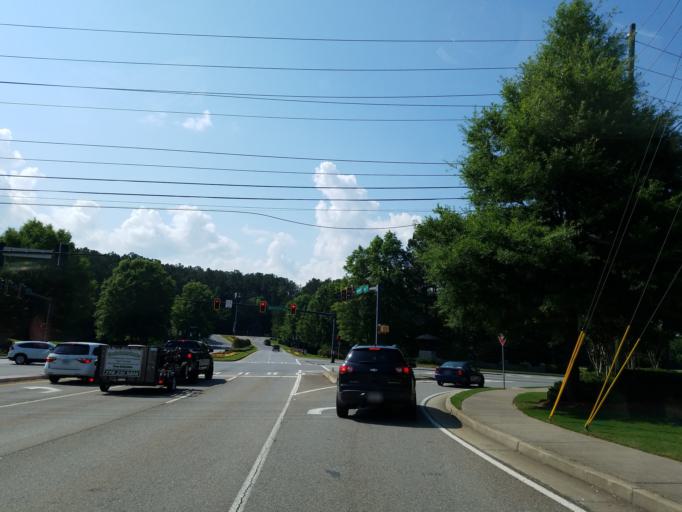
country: US
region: Georgia
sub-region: Cherokee County
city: Holly Springs
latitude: 34.1791
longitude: -84.5506
